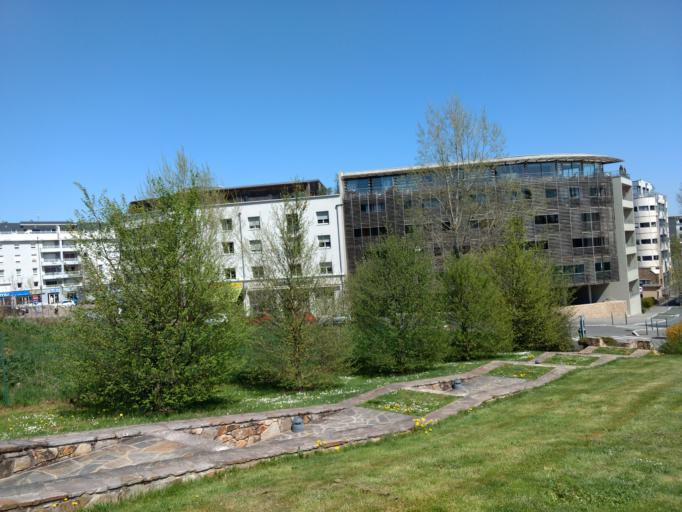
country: FR
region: Midi-Pyrenees
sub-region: Departement de l'Aveyron
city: Olemps
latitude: 44.3588
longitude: 2.5546
